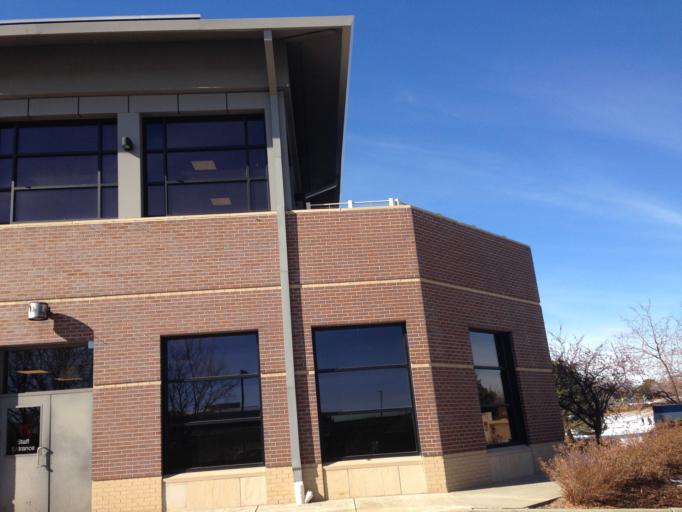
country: US
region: Colorado
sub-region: Broomfield County
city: Broomfield
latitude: 39.9176
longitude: -105.0686
